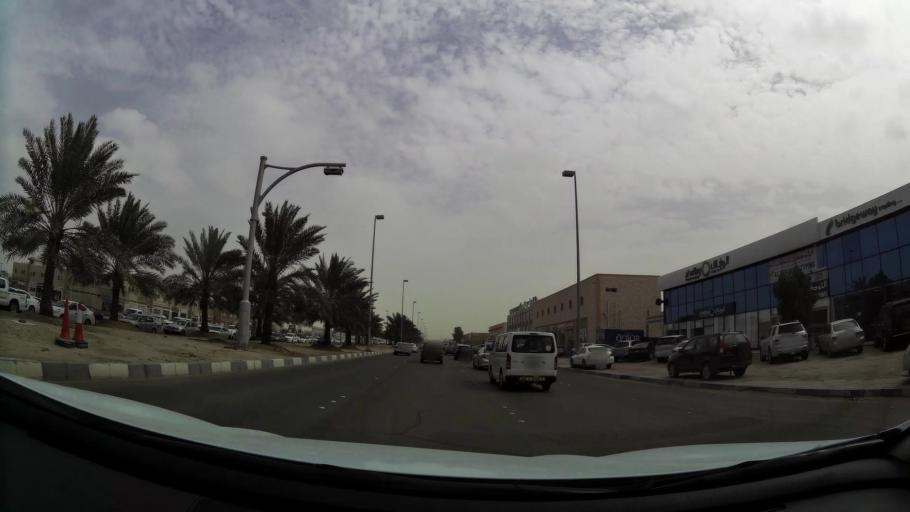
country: AE
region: Abu Dhabi
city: Abu Dhabi
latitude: 24.3728
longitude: 54.5022
